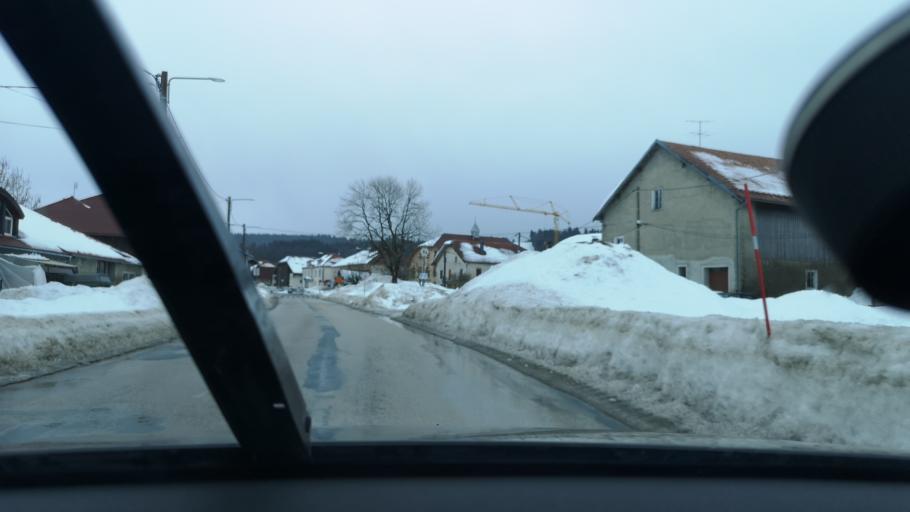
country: FR
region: Franche-Comte
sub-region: Departement du Doubs
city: Les Fourgs
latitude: 46.8364
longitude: 6.3983
